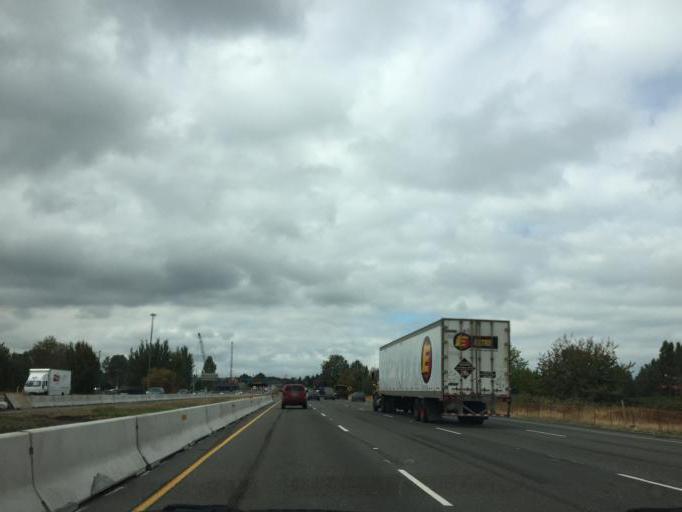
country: US
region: Washington
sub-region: Pierce County
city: Fife
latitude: 47.2414
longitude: -122.3861
